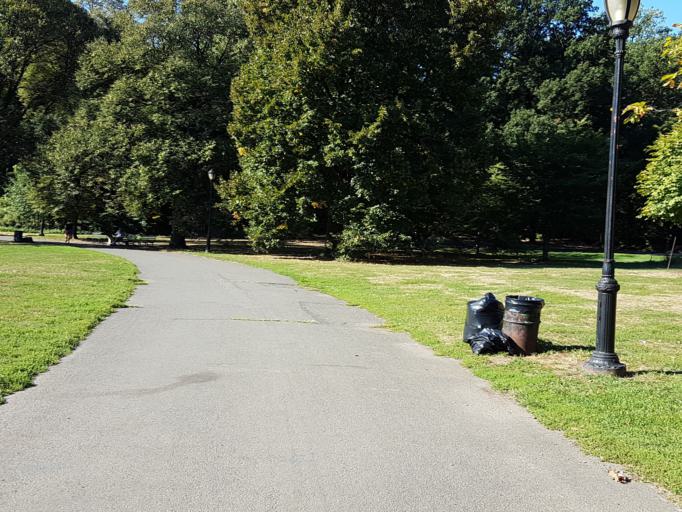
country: US
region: New York
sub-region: Kings County
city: Brooklyn
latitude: 40.6692
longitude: -73.9714
